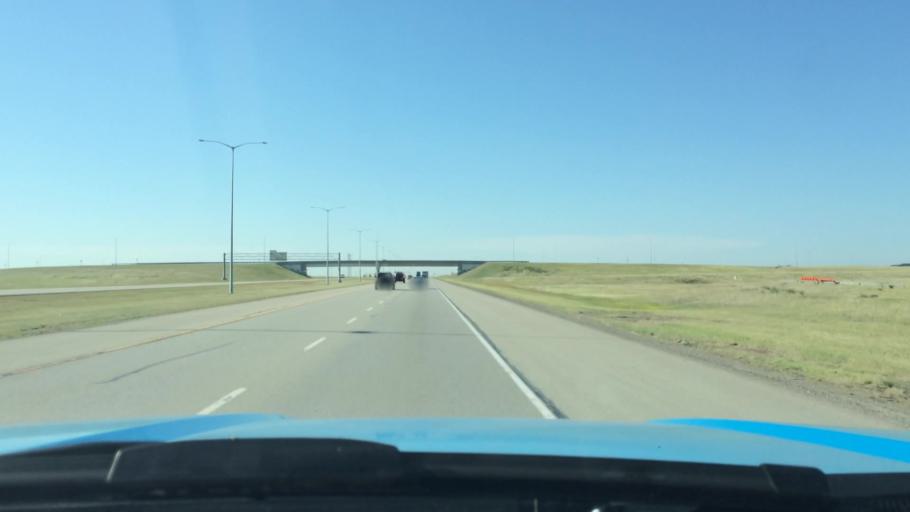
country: CA
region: Alberta
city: Chestermere
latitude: 51.1407
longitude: -113.9216
